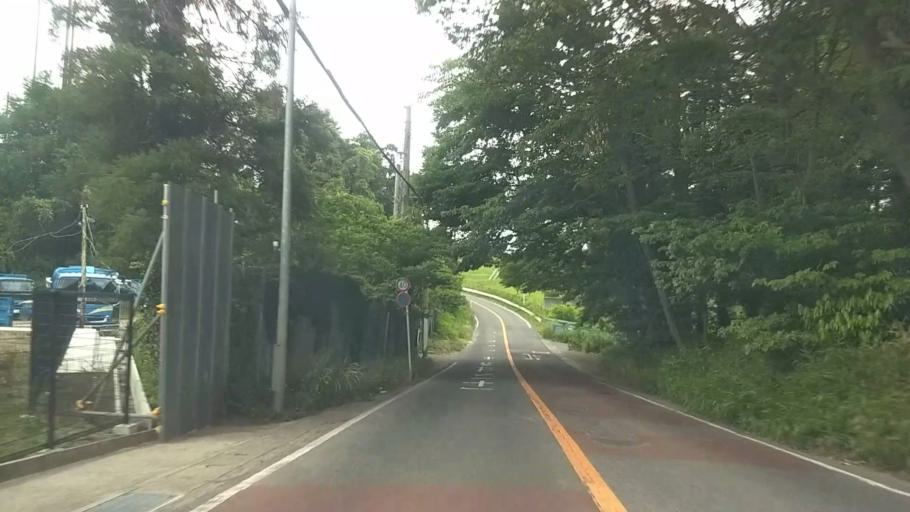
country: JP
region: Kanagawa
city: Fujisawa
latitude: 35.3591
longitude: 139.4355
